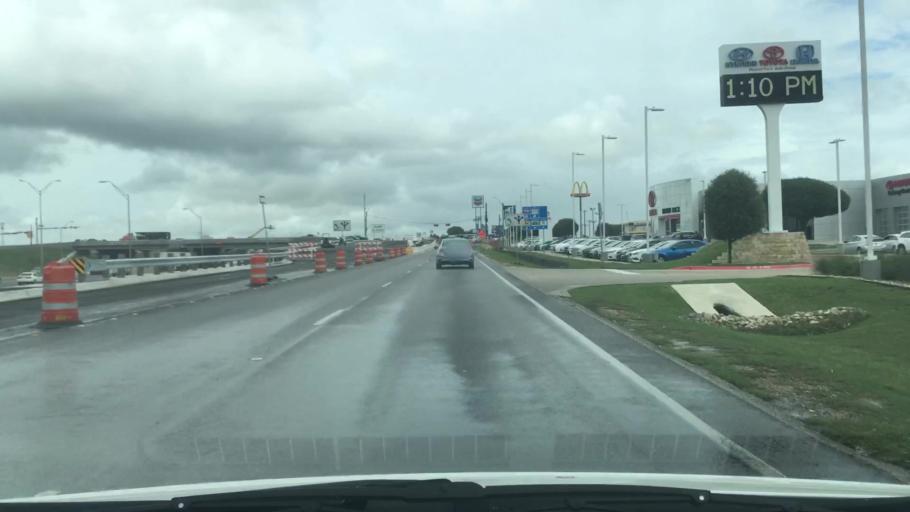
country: US
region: Texas
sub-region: Williamson County
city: Round Rock
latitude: 30.5328
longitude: -97.6912
